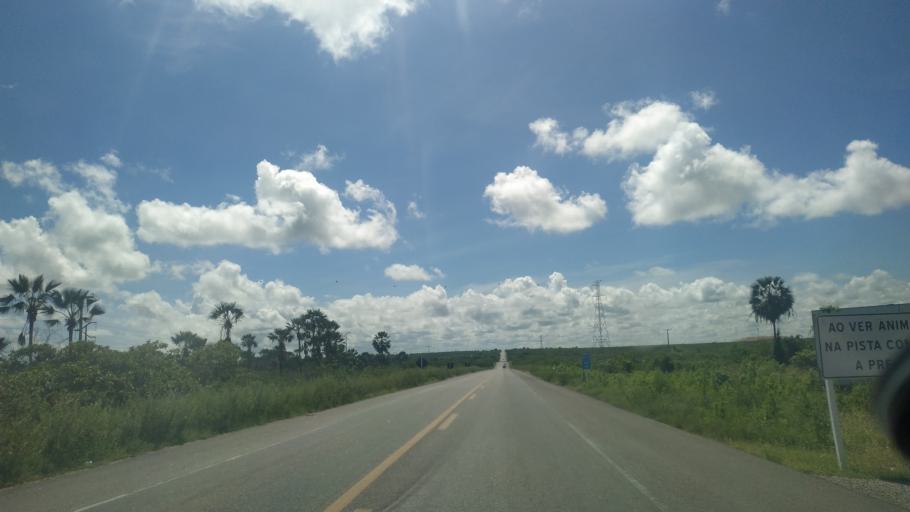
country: BR
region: Rio Grande do Norte
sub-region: Mossoro
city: Mossoro
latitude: -5.1825
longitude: -37.2971
